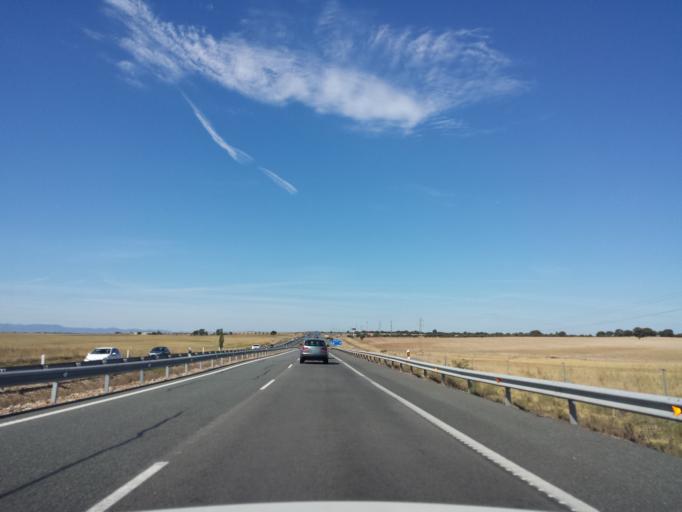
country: ES
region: Castille-La Mancha
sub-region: Province of Toledo
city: Calera y Chozas
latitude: 39.9299
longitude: -5.0122
